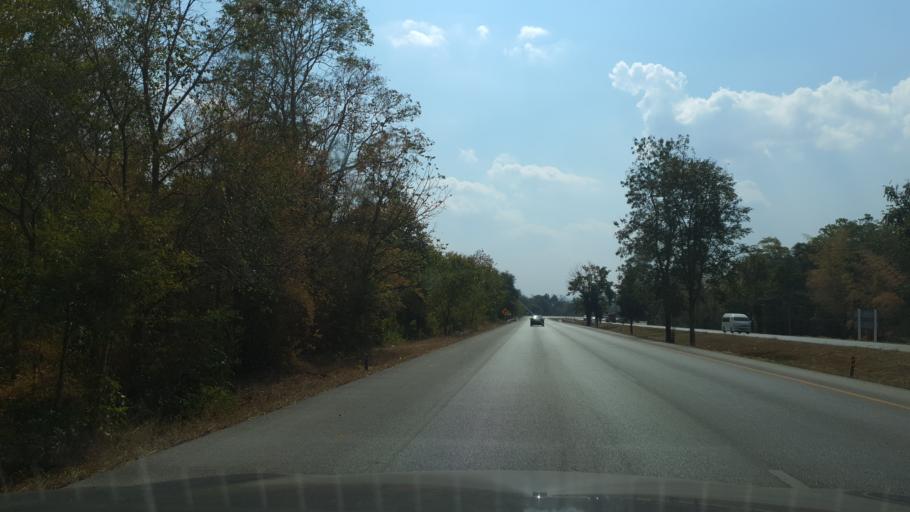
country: TH
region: Lampang
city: Mae Phrik
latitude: 17.4229
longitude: 99.1576
